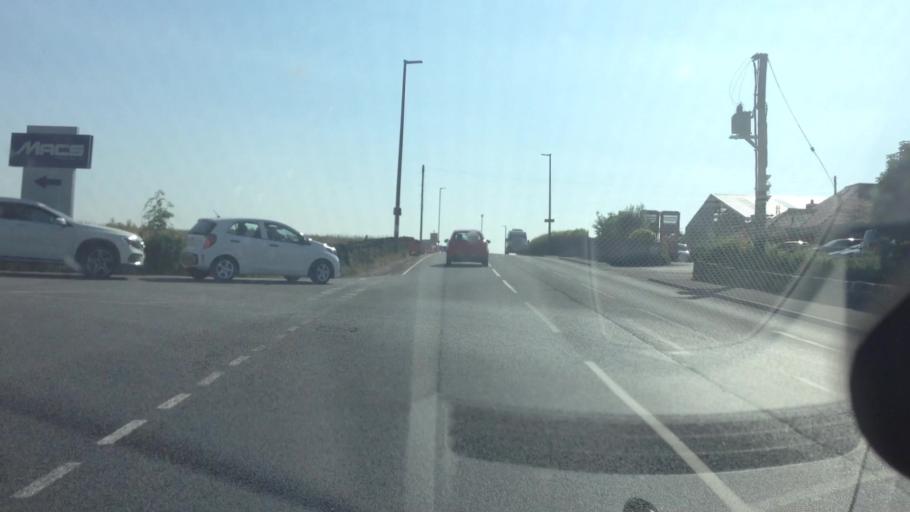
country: GB
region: England
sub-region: Calderdale
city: Elland
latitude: 53.6674
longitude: -1.8390
